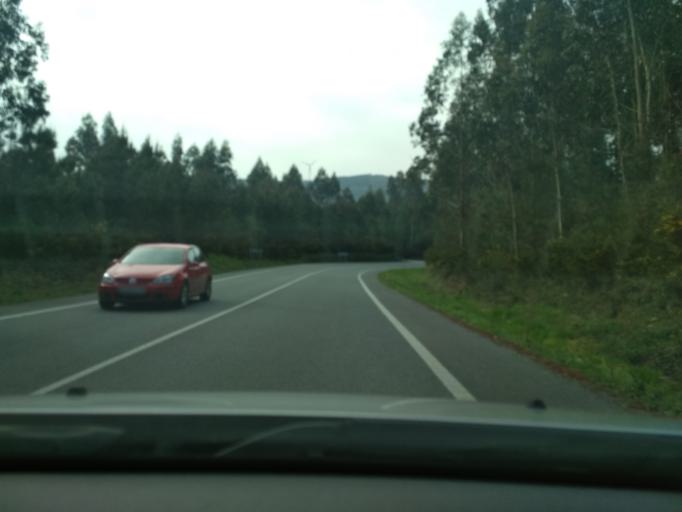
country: ES
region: Galicia
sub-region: Provincia de Pontevedra
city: Catoira
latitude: 42.6584
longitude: -8.7036
